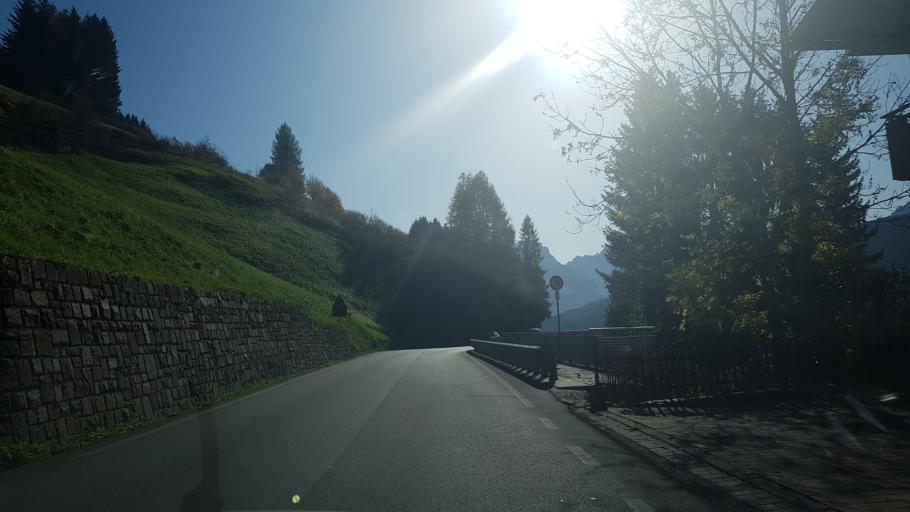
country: IT
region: Veneto
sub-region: Provincia di Belluno
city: Candide
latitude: 46.5959
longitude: 12.5000
